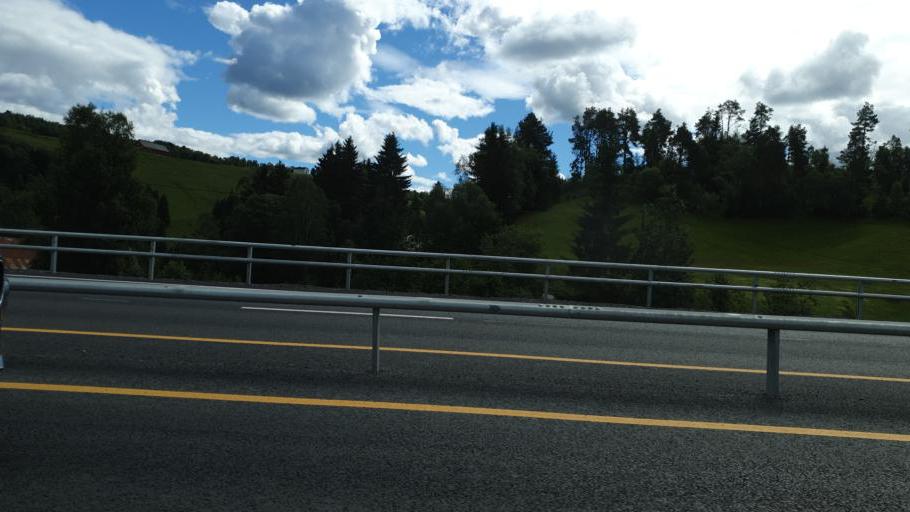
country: NO
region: Sor-Trondelag
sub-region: Midtre Gauldal
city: Storen
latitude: 62.9381
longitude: 10.1897
